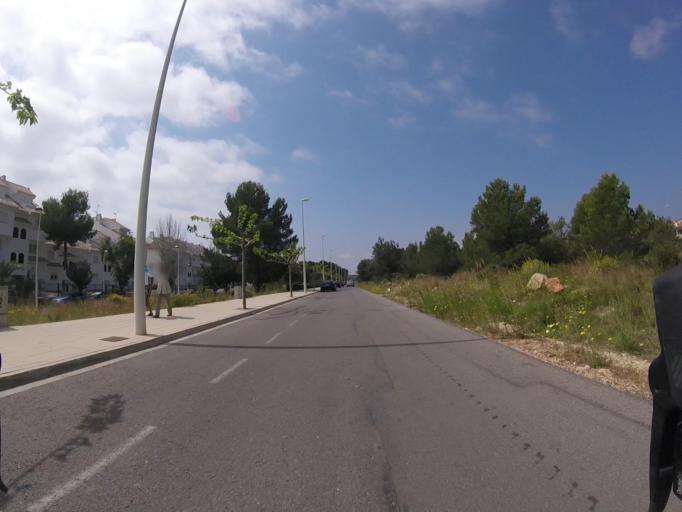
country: ES
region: Valencia
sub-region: Provincia de Castello
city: Alcoceber
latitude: 40.2507
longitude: 0.2782
